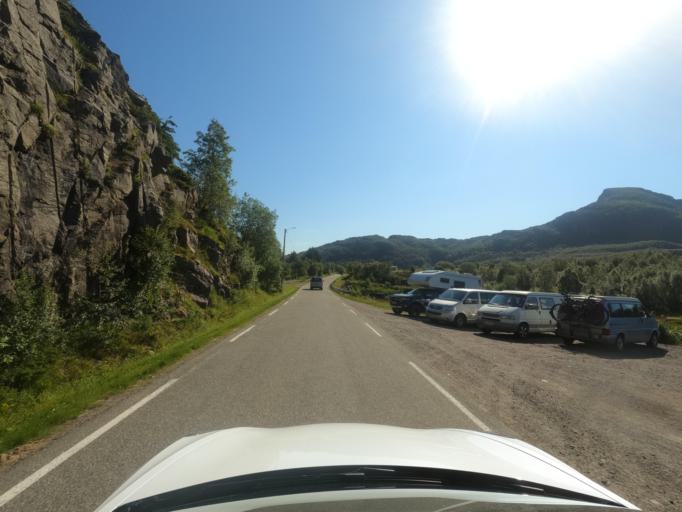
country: NO
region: Nordland
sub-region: Hadsel
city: Stokmarknes
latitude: 68.3039
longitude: 15.0116
